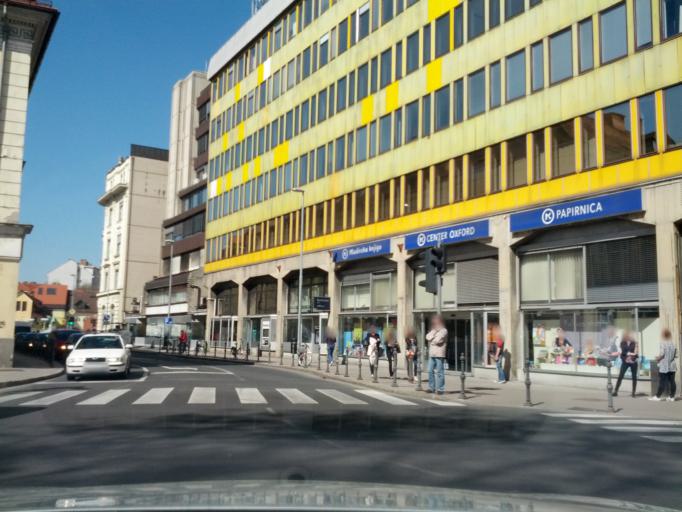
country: SI
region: Ljubljana
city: Ljubljana
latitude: 46.0508
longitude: 14.5096
